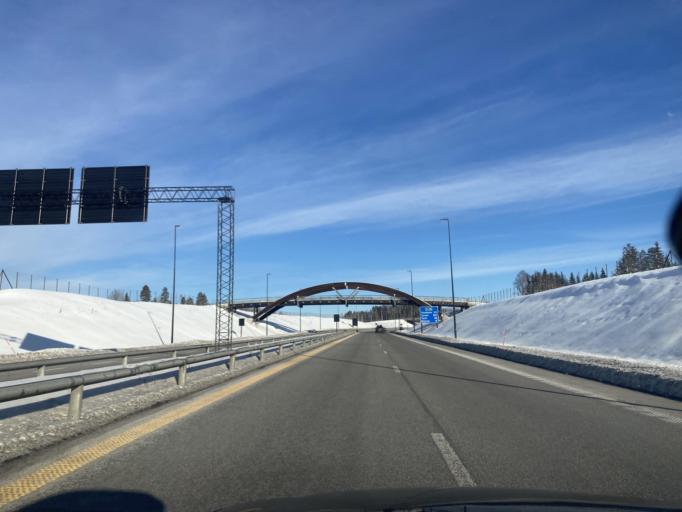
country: NO
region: Hedmark
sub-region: Loten
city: Loten
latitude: 60.8299
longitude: 11.2931
